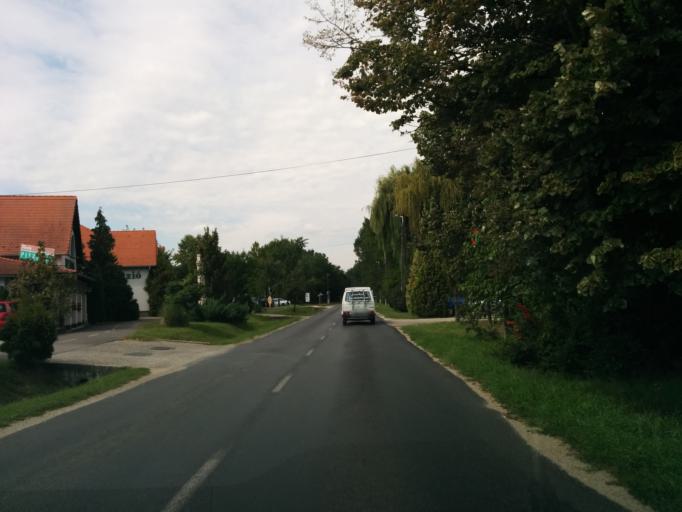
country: HU
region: Gyor-Moson-Sopron
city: Fertod
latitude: 47.6214
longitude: 16.7867
